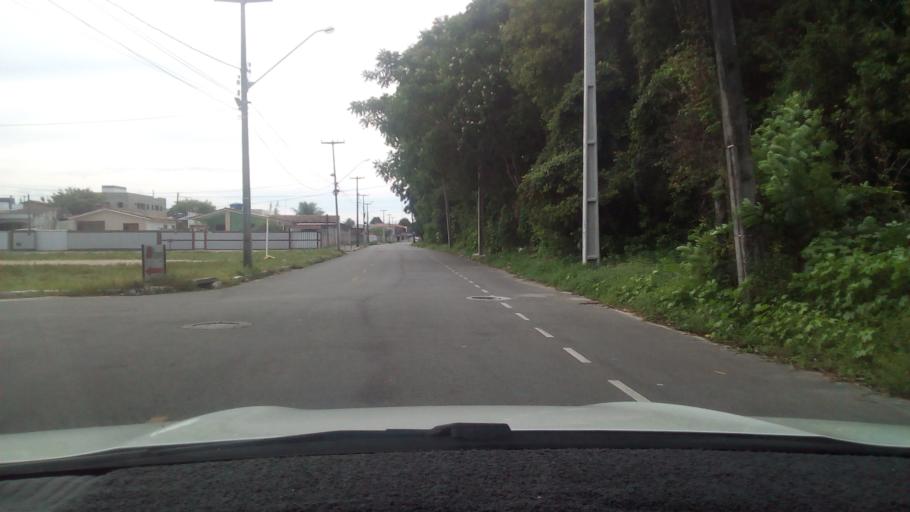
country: BR
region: Paraiba
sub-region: Joao Pessoa
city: Joao Pessoa
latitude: -7.1616
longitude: -34.8643
